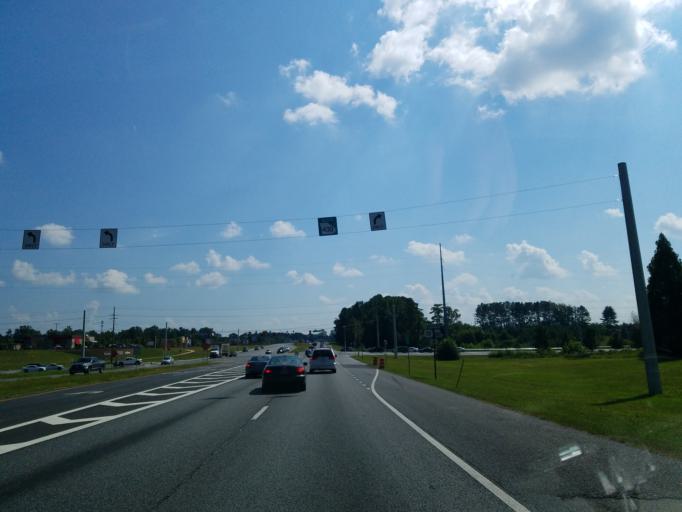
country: US
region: Georgia
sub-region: Dawson County
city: Dawsonville
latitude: 34.3548
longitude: -84.0465
